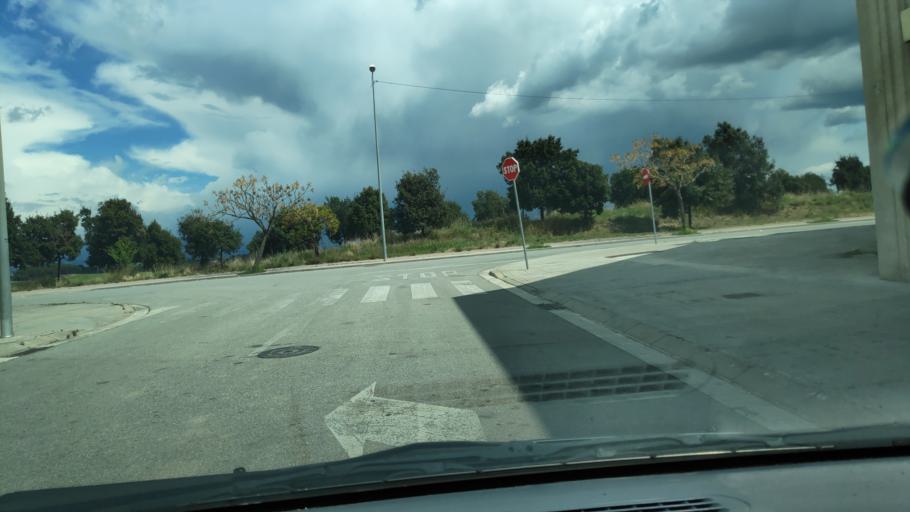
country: ES
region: Catalonia
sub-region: Provincia de Barcelona
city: Polinya
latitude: 41.5424
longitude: 2.1365
